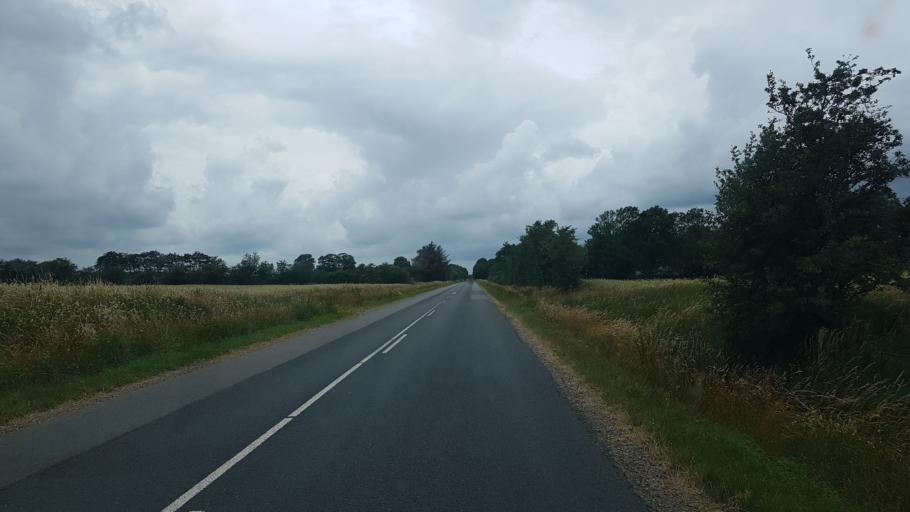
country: DK
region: South Denmark
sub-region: Kolding Kommune
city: Vamdrup
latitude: 55.4314
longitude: 9.2375
